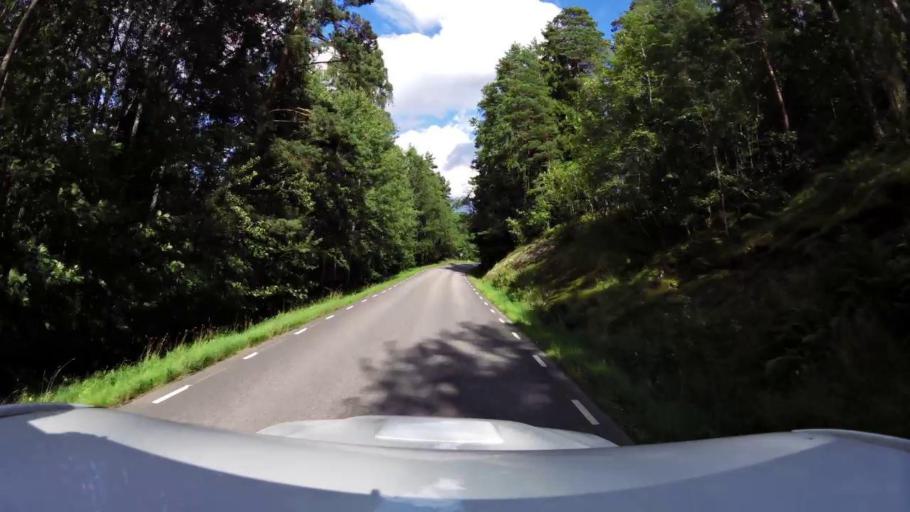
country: SE
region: OEstergoetland
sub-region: Kinda Kommun
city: Rimforsa
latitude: 58.2265
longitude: 15.7125
